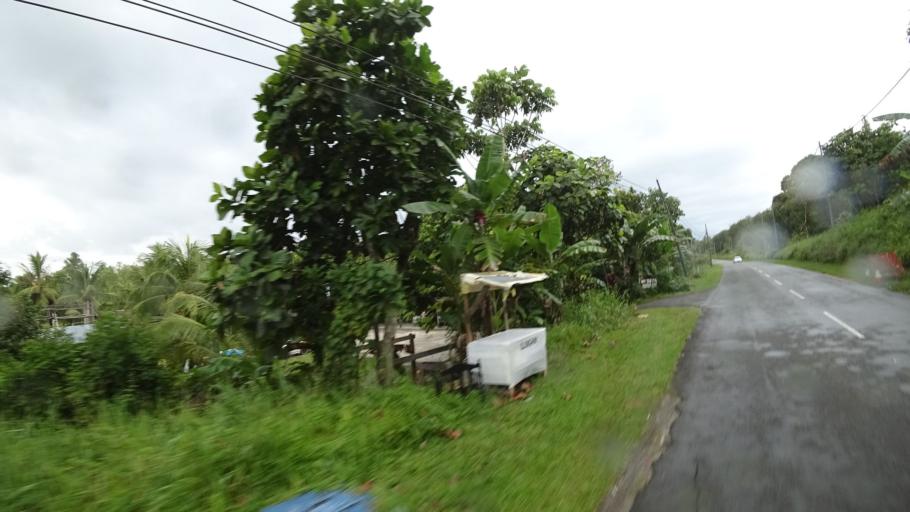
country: BN
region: Brunei and Muara
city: Bandar Seri Begawan
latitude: 4.8440
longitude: 114.9522
